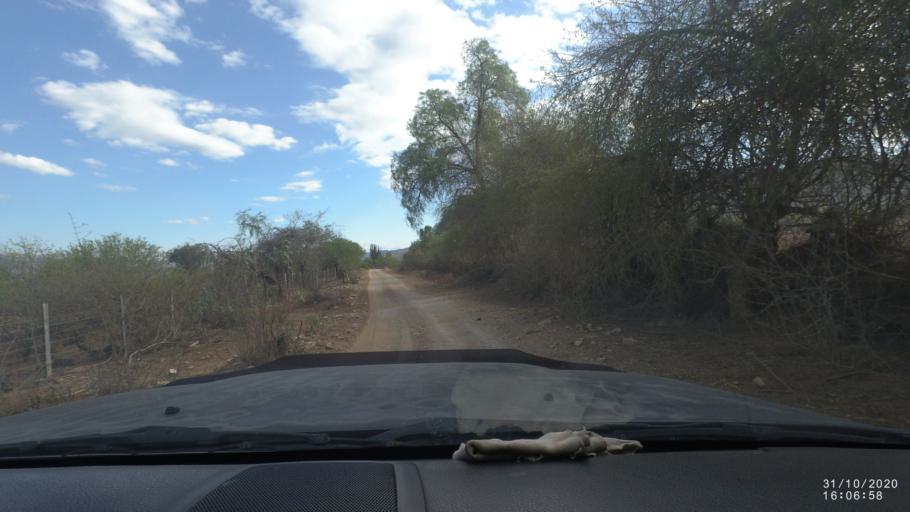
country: BO
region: Chuquisaca
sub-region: Provincia Zudanez
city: Mojocoya
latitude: -18.3769
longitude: -64.6457
